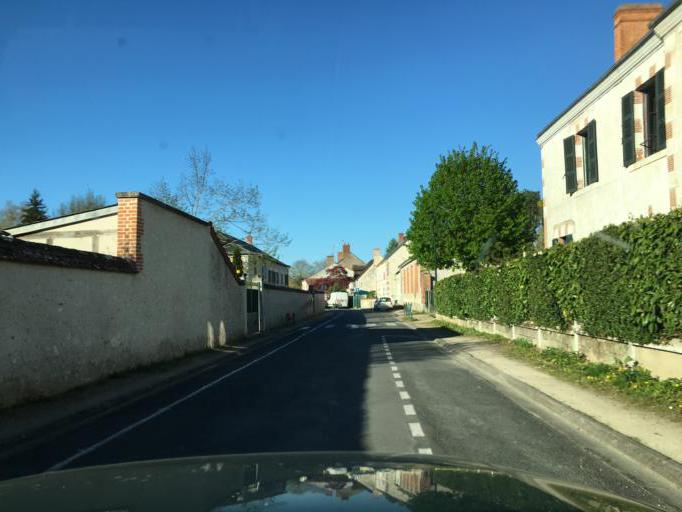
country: FR
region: Centre
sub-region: Departement du Loiret
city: Lailly-en-Val
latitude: 47.7678
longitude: 1.6849
